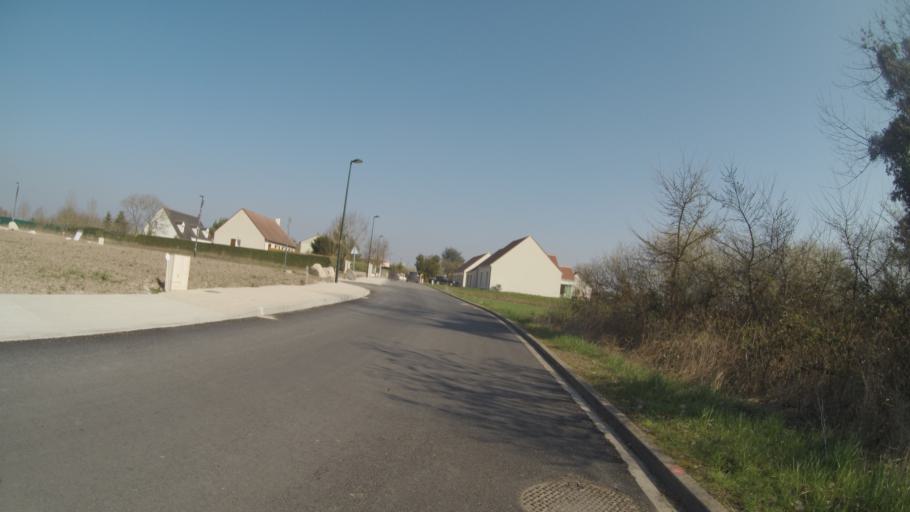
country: FR
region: Centre
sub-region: Departement du Loiret
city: Mardie
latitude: 47.8874
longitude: 2.0494
